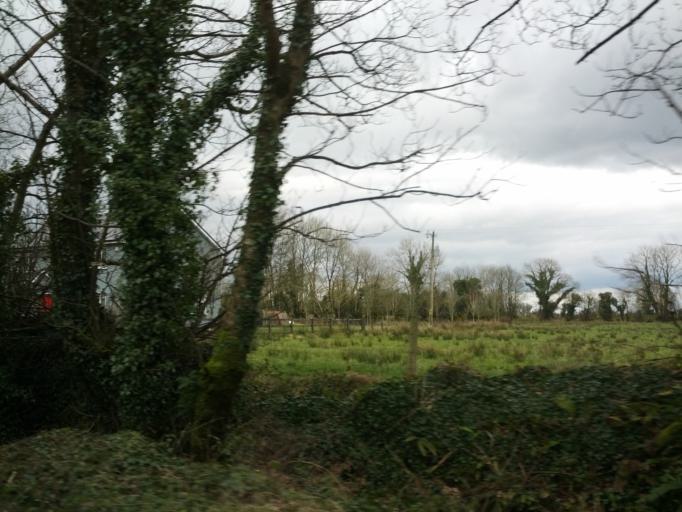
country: IE
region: Connaught
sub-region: County Galway
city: Athenry
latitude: 53.4368
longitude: -8.6379
